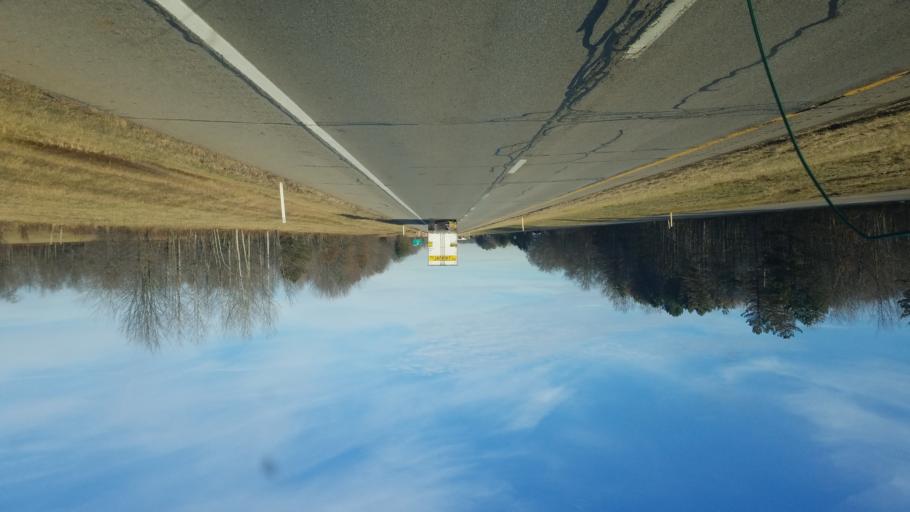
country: US
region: Ohio
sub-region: Ashtabula County
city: Orwell
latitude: 41.5216
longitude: -80.7132
